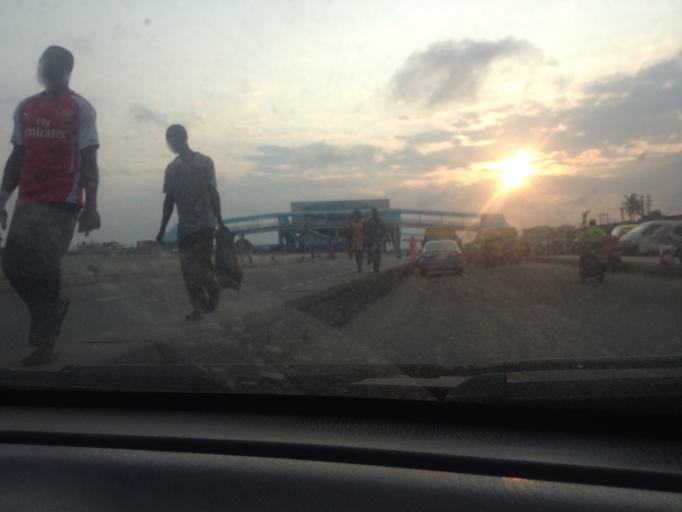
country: NG
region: Lagos
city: Ajegunle
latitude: 6.4601
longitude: 3.3141
